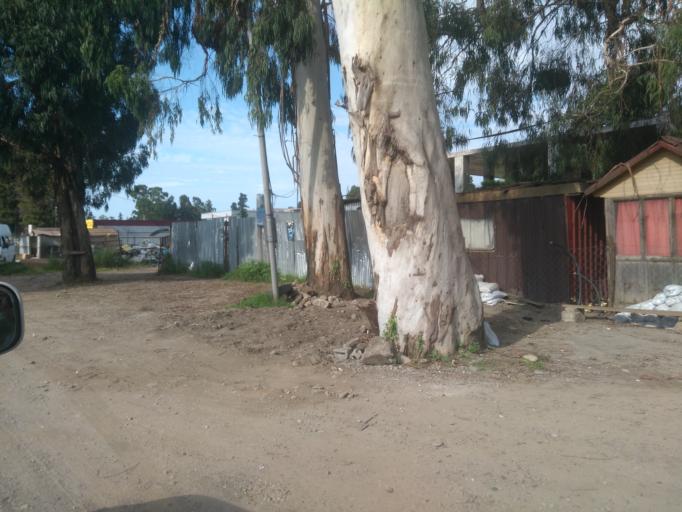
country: GE
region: Ajaria
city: Batumi
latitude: 41.6089
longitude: 41.6265
